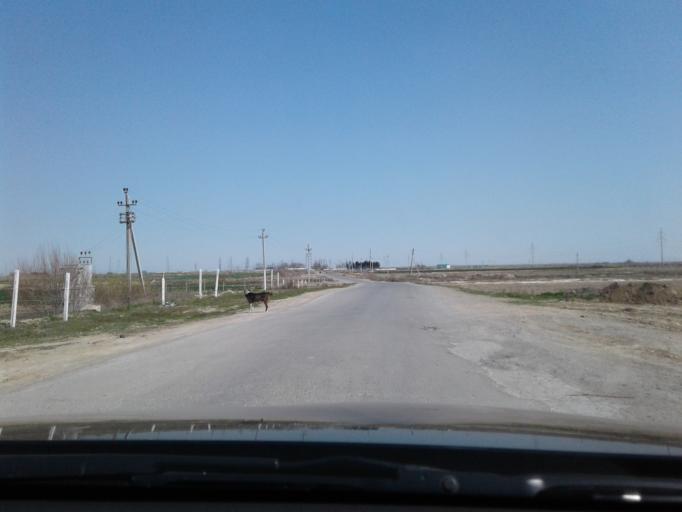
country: TM
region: Ahal
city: Abadan
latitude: 38.0969
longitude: 58.2010
